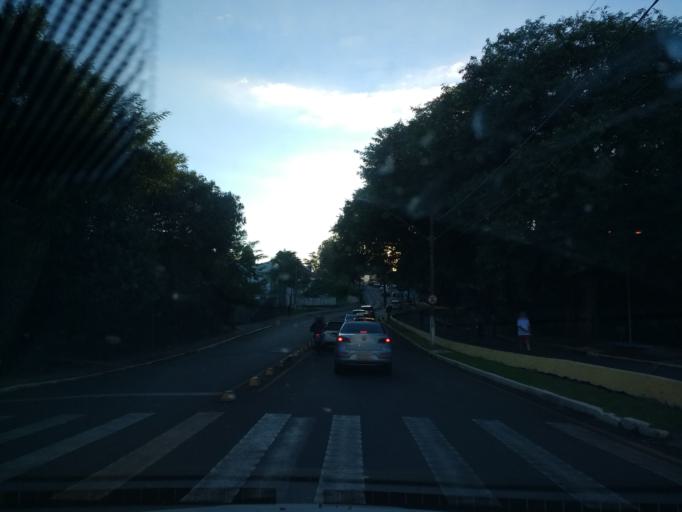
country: BR
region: Parana
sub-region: Londrina
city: Londrina
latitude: -23.3270
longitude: -51.1638
